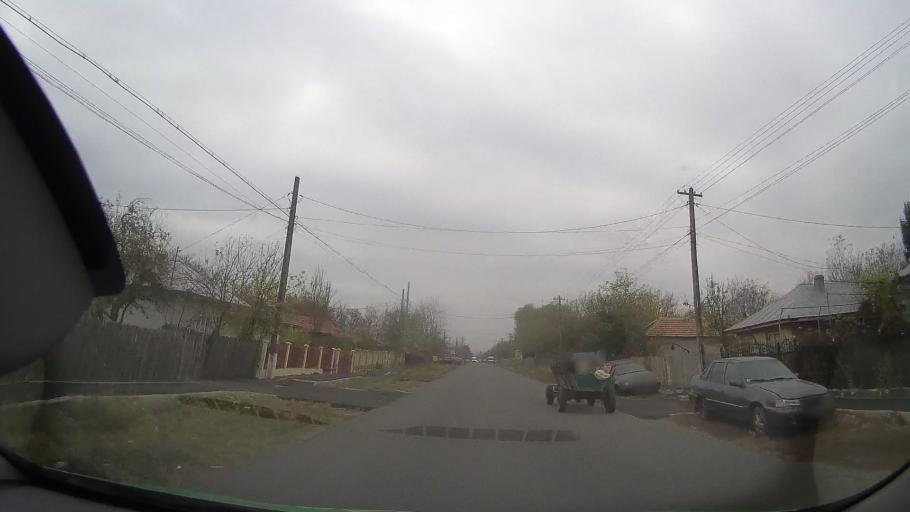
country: RO
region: Buzau
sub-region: Comuna Pogoanele
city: Pogoanele
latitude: 44.9255
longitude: 26.9955
